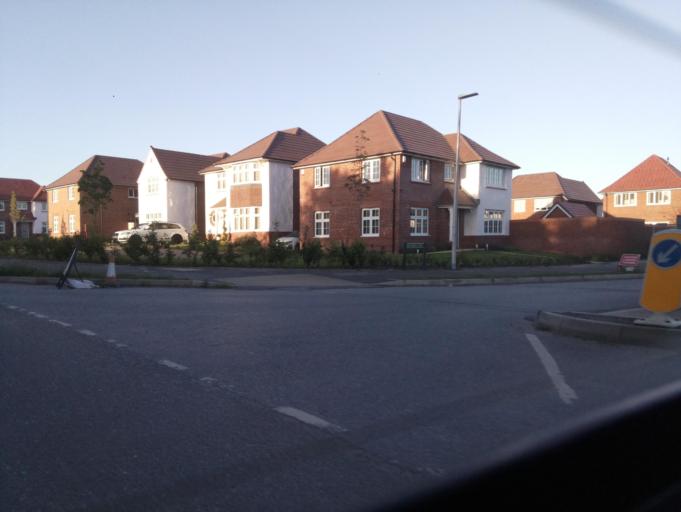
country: GB
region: England
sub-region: Devon
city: Newton Abbot
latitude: 50.5523
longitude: -3.6076
